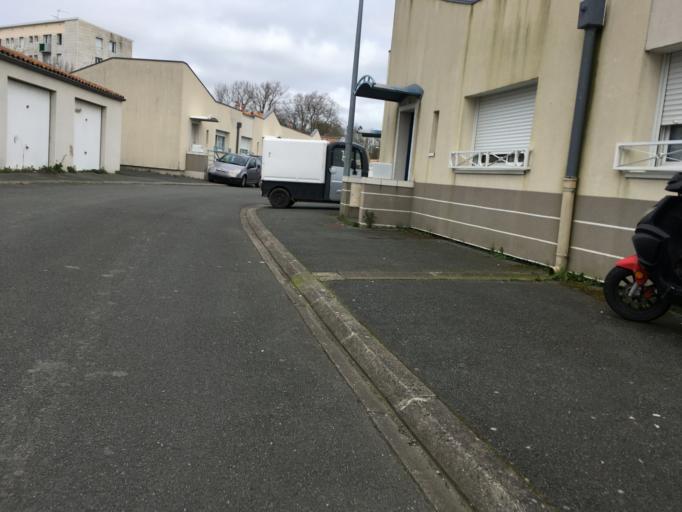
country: FR
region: Poitou-Charentes
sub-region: Departement de la Charente-Maritime
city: La Rochelle
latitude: 46.1752
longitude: -1.1462
